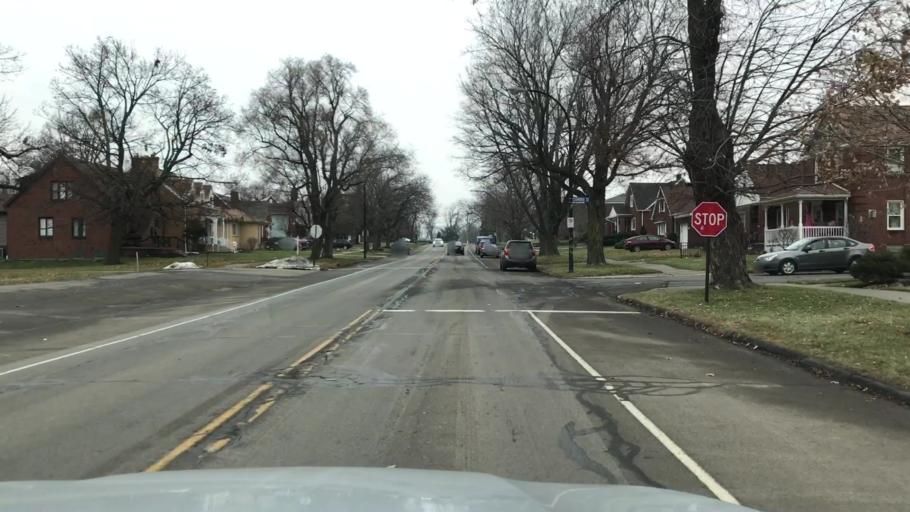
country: US
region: New York
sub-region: Erie County
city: Lackawanna
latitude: 42.8256
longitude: -78.8100
